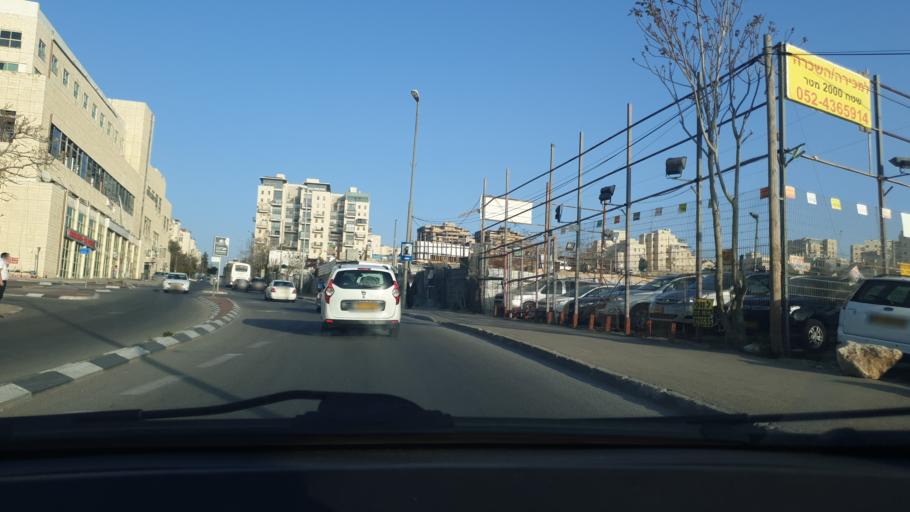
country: PS
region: West Bank
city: Bayt Iksa
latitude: 31.7933
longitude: 35.1876
